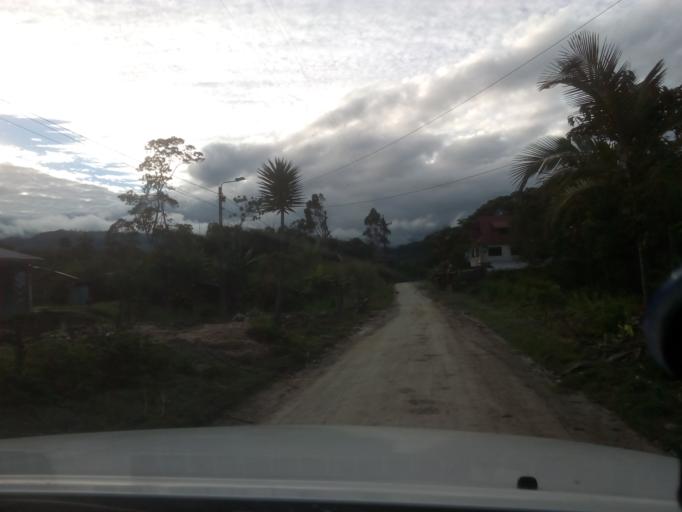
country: PE
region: Pasco
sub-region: Provincia de Oxapampa
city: Villa Rica
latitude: -10.7635
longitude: -75.2615
